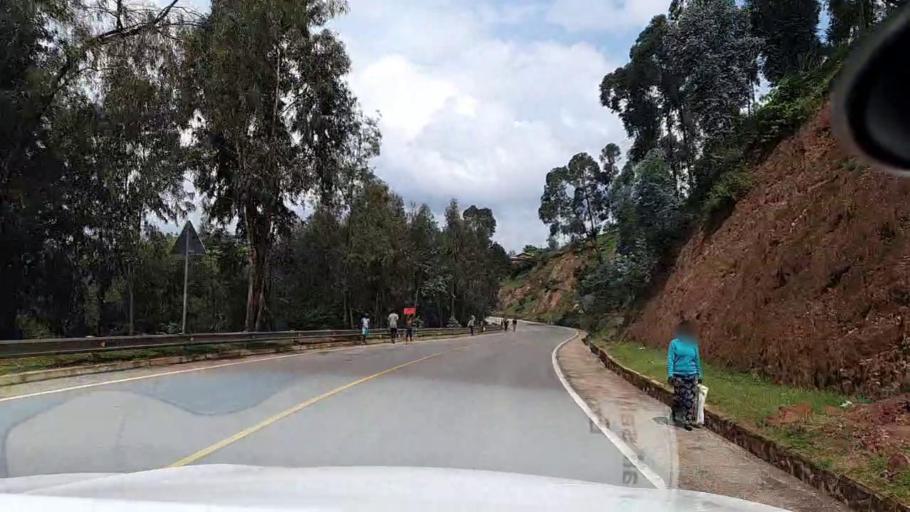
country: RW
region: Southern Province
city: Nzega
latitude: -2.4840
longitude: 29.5221
